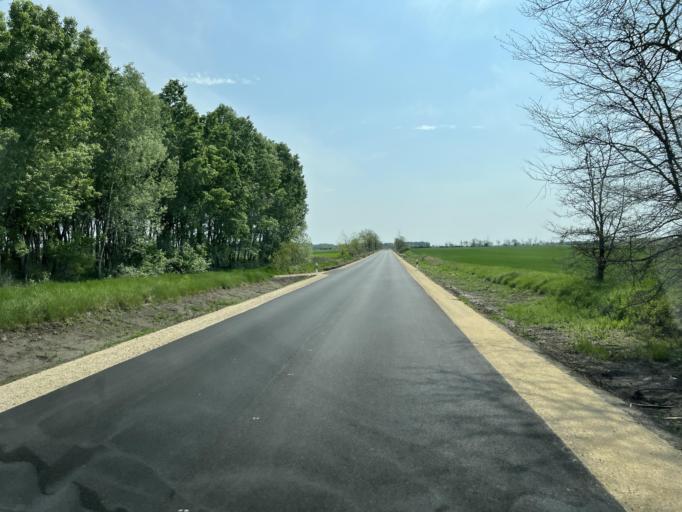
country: HU
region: Pest
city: Nagykoros
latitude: 47.0246
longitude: 19.8252
